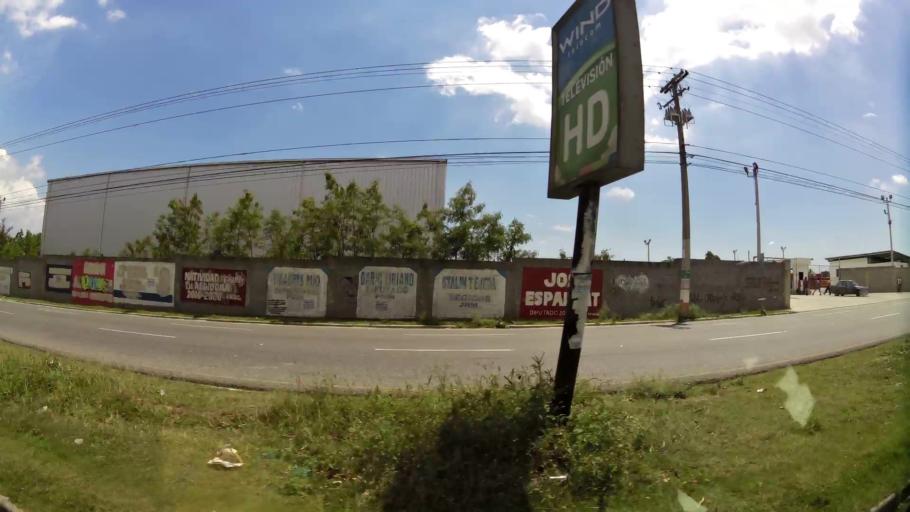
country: DO
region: Nacional
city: Ensanche Luperon
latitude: 18.5454
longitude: -69.8699
